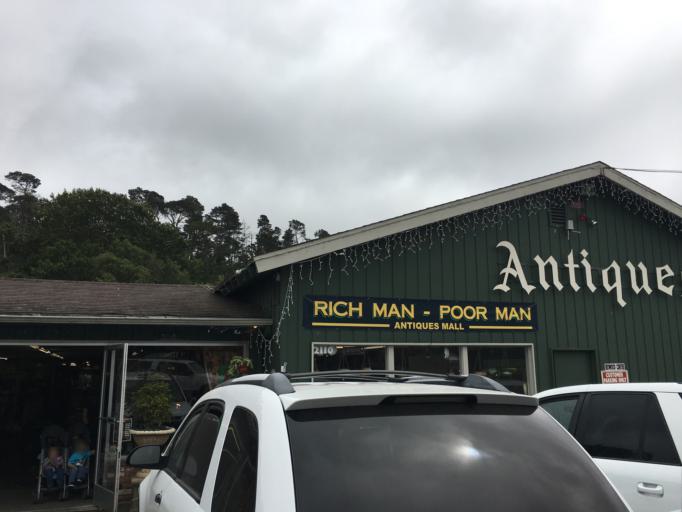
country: US
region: California
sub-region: San Luis Obispo County
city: Cambria
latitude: 35.5631
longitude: -121.0838
